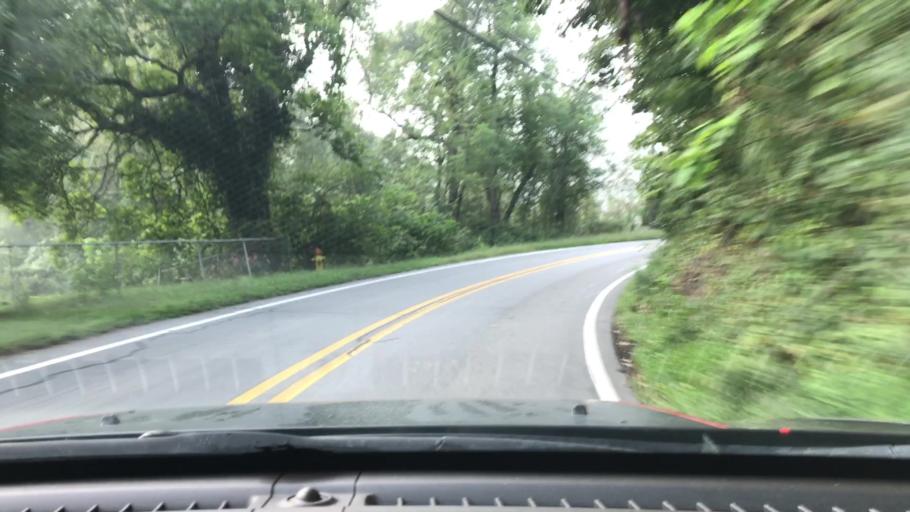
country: US
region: North Carolina
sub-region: Buncombe County
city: Woodfin
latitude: 35.6256
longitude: -82.6047
